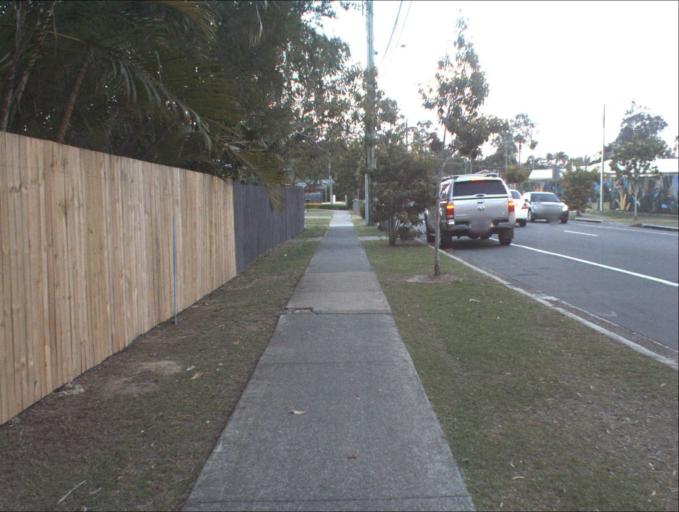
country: AU
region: Queensland
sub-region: Logan
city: Waterford West
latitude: -27.6767
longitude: 153.1315
